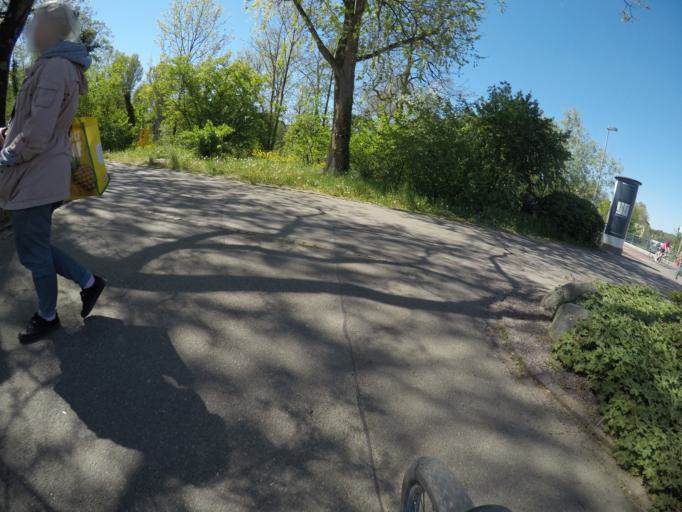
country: DE
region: Baden-Wuerttemberg
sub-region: Regierungsbezirk Stuttgart
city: Waiblingen
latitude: 48.8334
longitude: 9.3204
